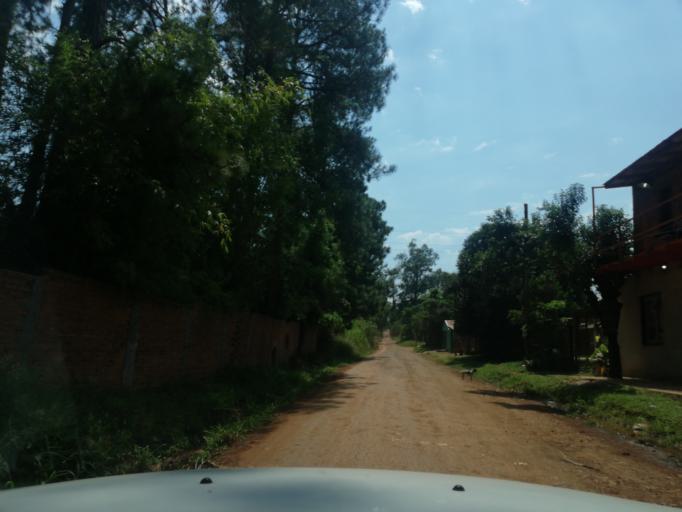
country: AR
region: Misiones
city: Garupa
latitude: -27.4436
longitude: -55.8897
